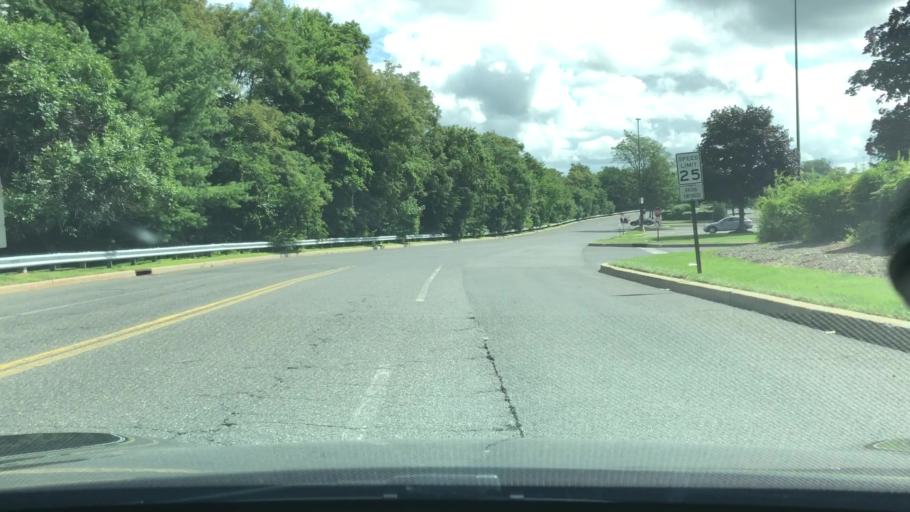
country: US
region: New Jersey
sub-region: Monmouth County
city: West Freehold
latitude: 40.2560
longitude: -74.3015
